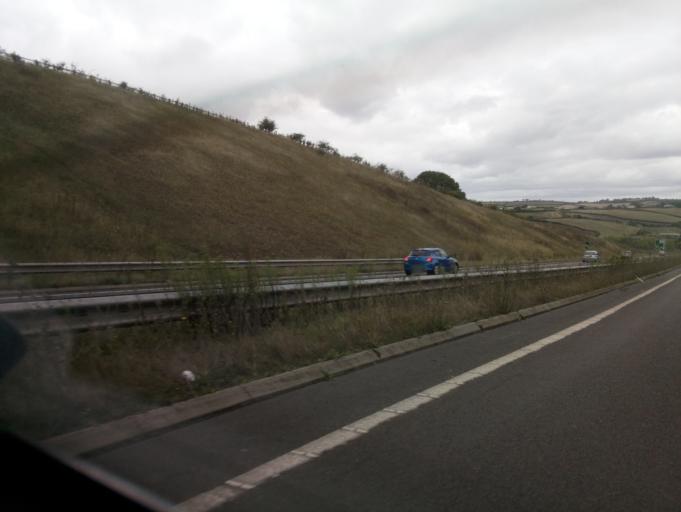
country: GB
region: England
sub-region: Devon
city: Kingskerswell
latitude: 50.4829
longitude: -3.5752
